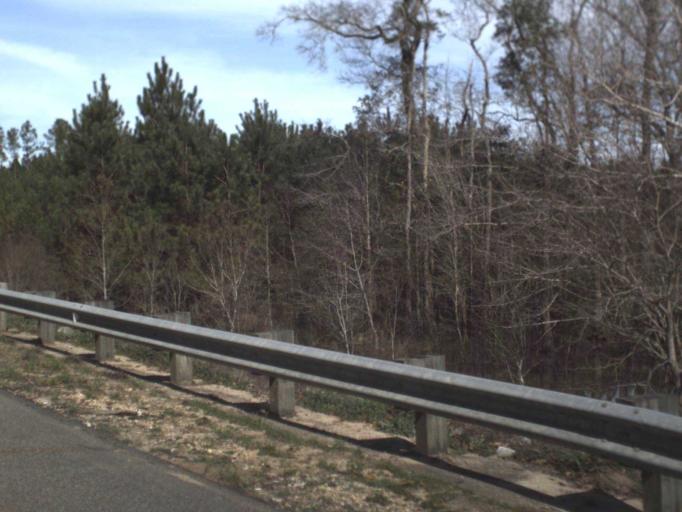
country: US
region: Florida
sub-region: Washington County
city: Chipley
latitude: 30.8354
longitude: -85.5329
